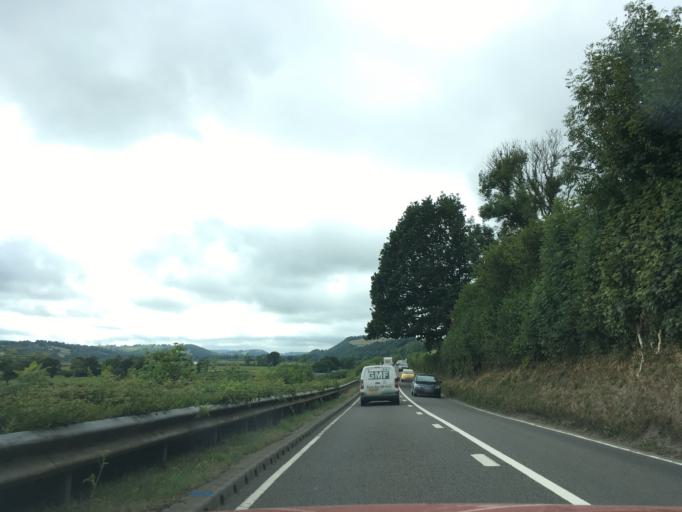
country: GB
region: Wales
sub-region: Carmarthenshire
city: Llanddarog
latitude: 51.8731
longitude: -4.1954
